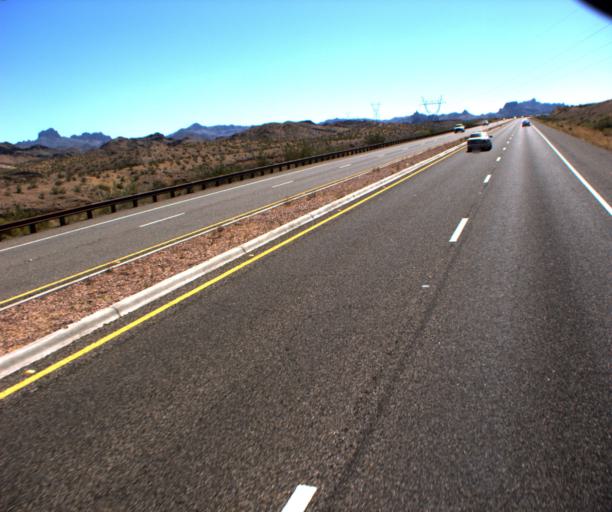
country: US
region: Nevada
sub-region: Clark County
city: Laughlin
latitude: 35.1901
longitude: -114.5146
